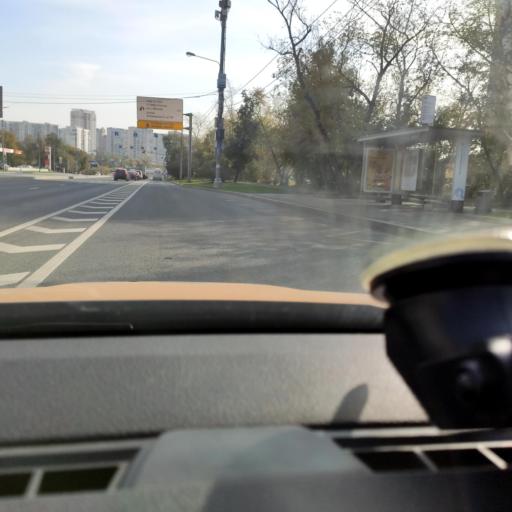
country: RU
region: Moscow
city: Amin'yevo
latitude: 55.6929
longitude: 37.4738
